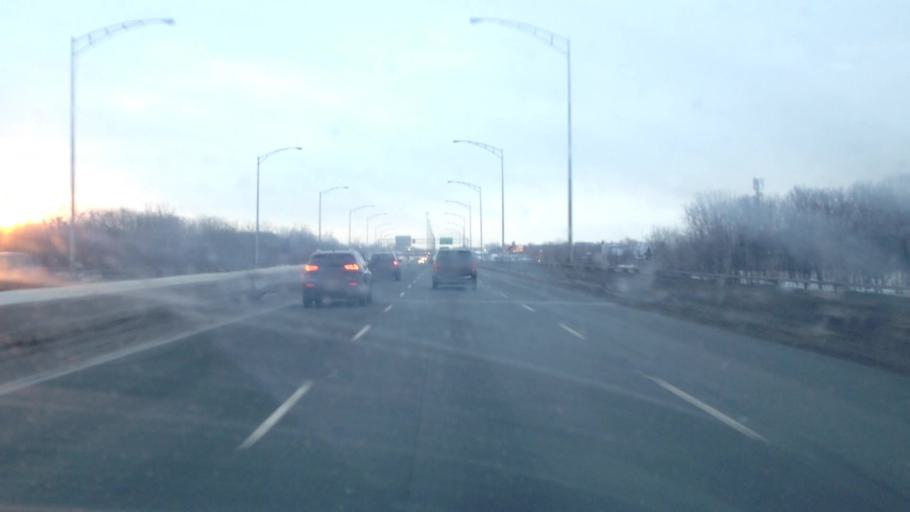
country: CA
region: Quebec
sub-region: Laurentides
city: Boisbriand
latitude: 45.5805
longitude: -73.8374
